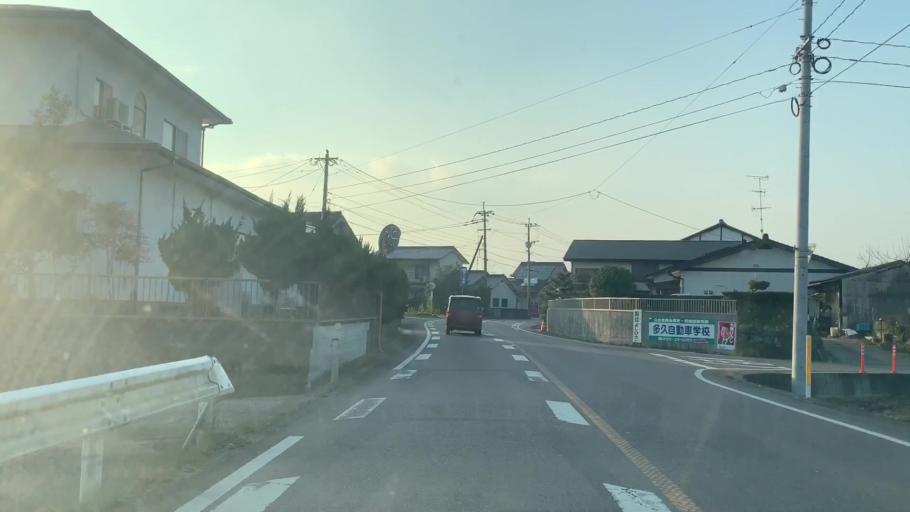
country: JP
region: Saga Prefecture
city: Saga-shi
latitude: 33.2797
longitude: 130.1602
